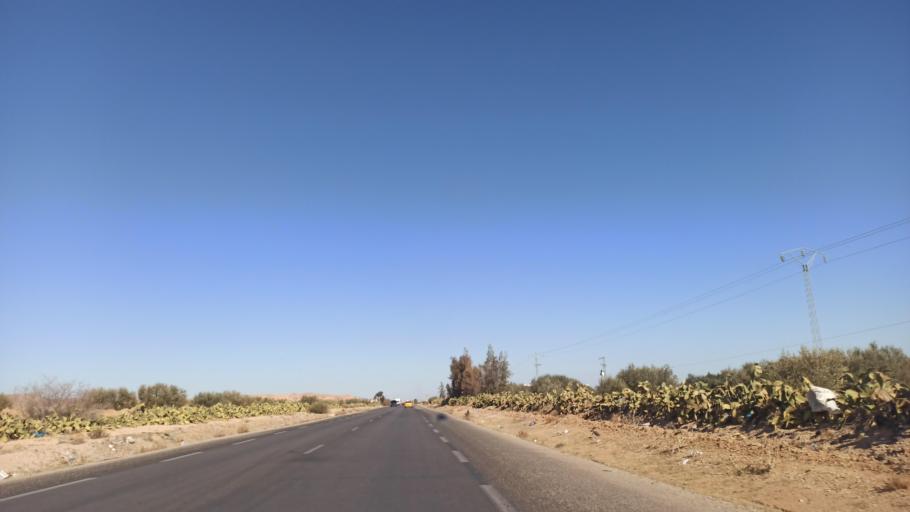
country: TN
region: Sidi Bu Zayd
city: Bi'r al Hufayy
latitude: 34.8974
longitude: 9.1730
